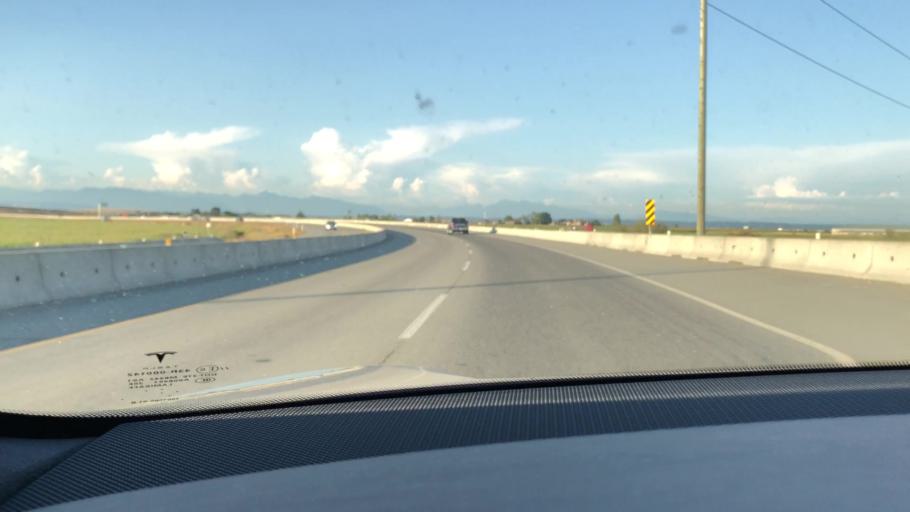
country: CA
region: British Columbia
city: Ladner
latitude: 49.0608
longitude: -123.0380
